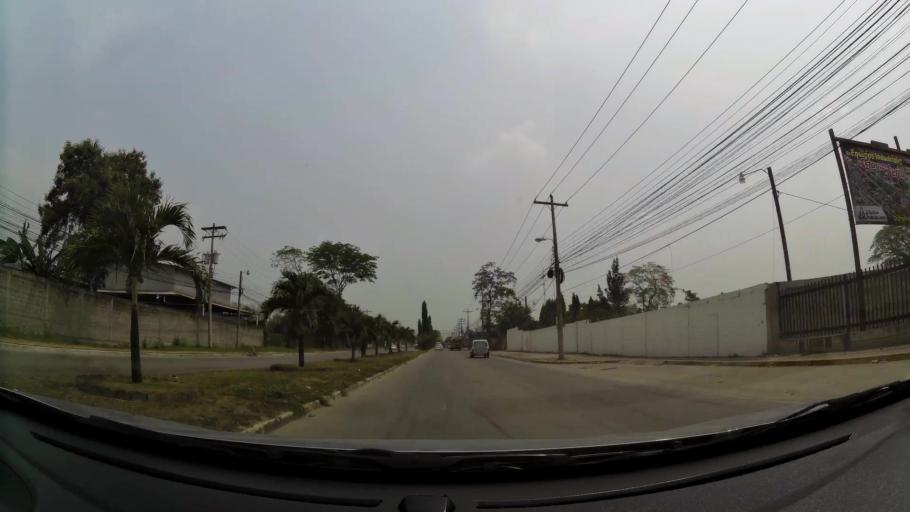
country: HN
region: Cortes
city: San Pedro Sula
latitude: 15.4837
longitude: -88.0249
